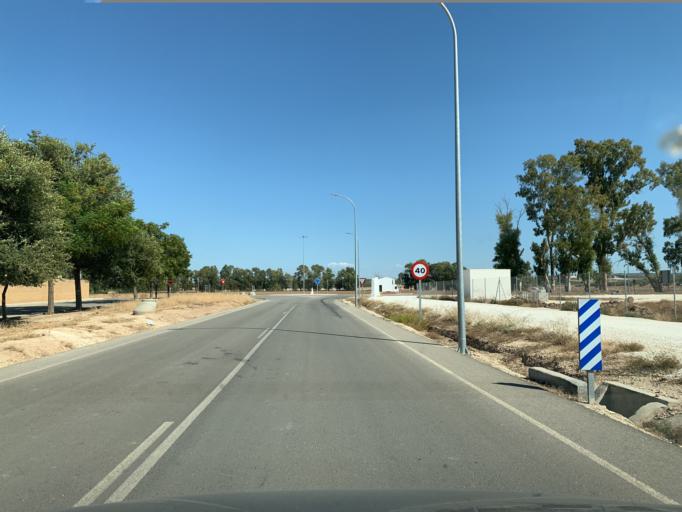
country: ES
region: Andalusia
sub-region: Provincia de Sevilla
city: El Rubio
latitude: 37.3496
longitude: -4.9870
